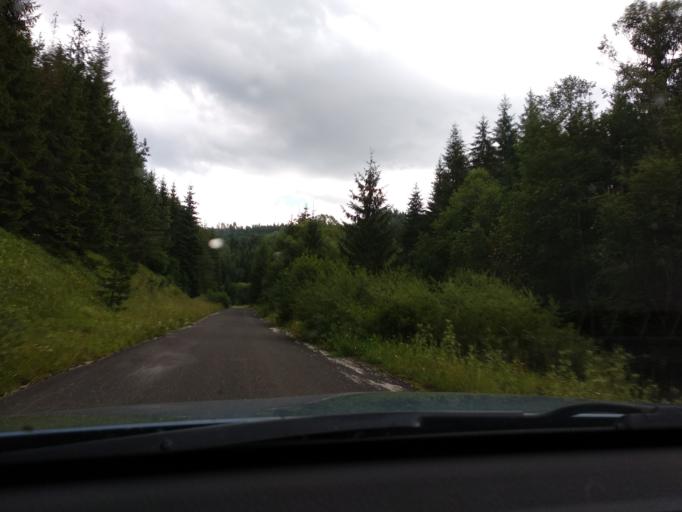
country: SK
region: Zilinsky
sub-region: Okres Liptovsky Mikulas
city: Hybe
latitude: 49.0243
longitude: 19.8761
